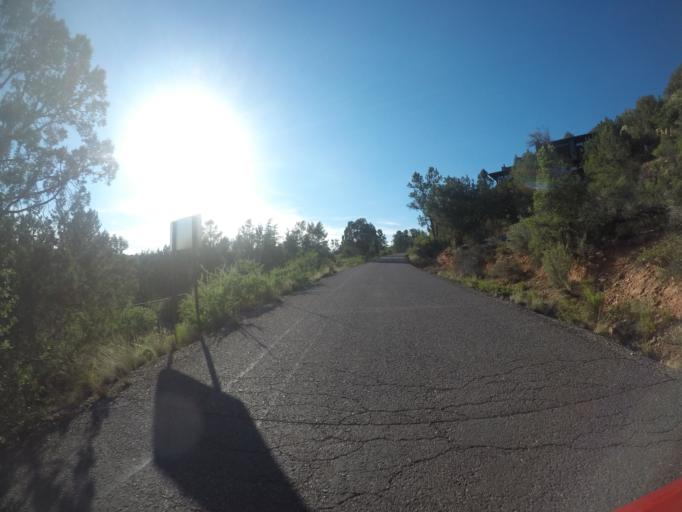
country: US
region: Arizona
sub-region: Yavapai County
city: West Sedona
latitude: 34.8281
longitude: -111.7931
